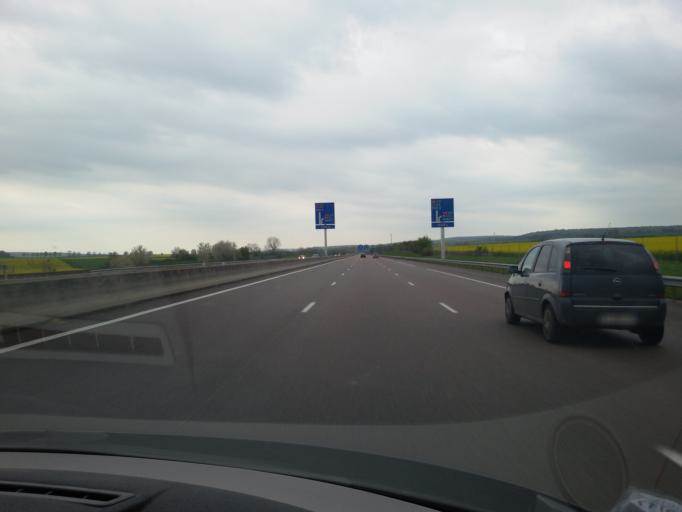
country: FR
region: Champagne-Ardenne
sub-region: Departement de la Haute-Marne
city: Rolampont
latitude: 47.8986
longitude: 5.2239
